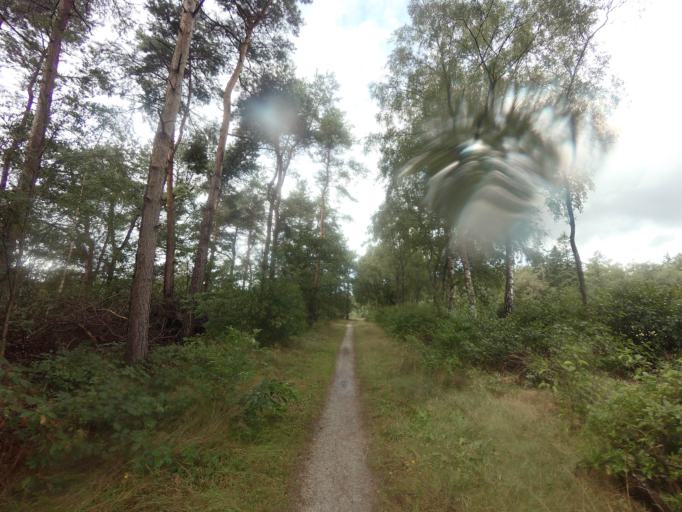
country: NL
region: Overijssel
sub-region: Gemeente Staphorst
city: Staphorst
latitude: 52.6123
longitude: 6.3324
